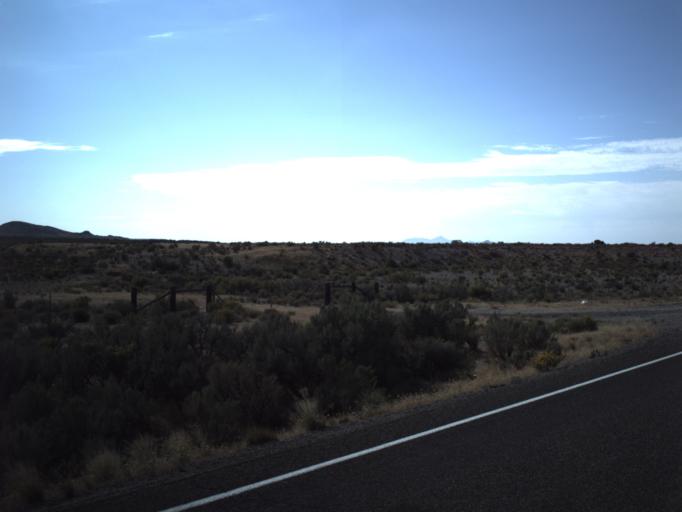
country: US
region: Idaho
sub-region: Cassia County
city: Burley
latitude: 41.6592
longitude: -113.5484
